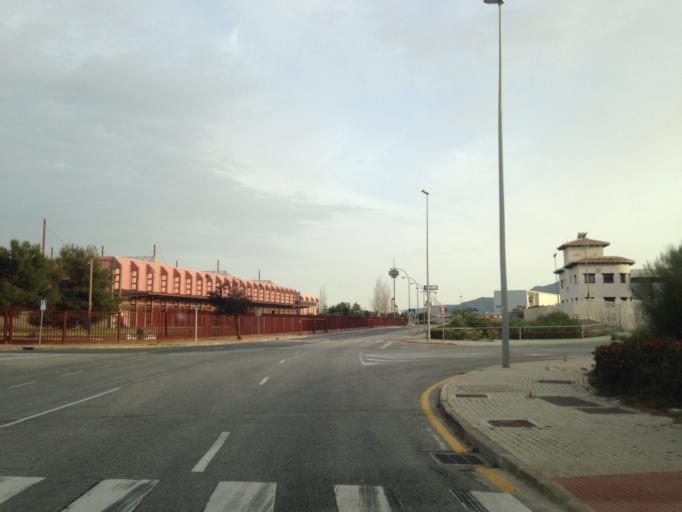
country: ES
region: Andalusia
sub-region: Provincia de Malaga
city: Alhaurin de la Torre
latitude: 36.7152
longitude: -4.5170
